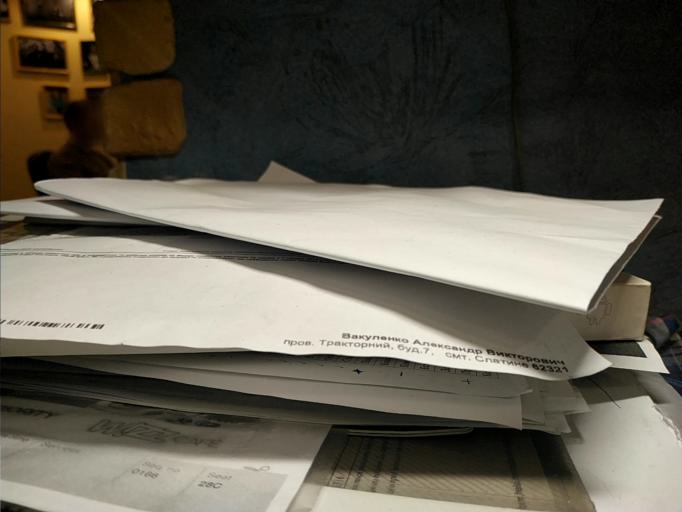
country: RU
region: Tverskaya
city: Zubtsov
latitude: 56.1042
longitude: 34.6649
